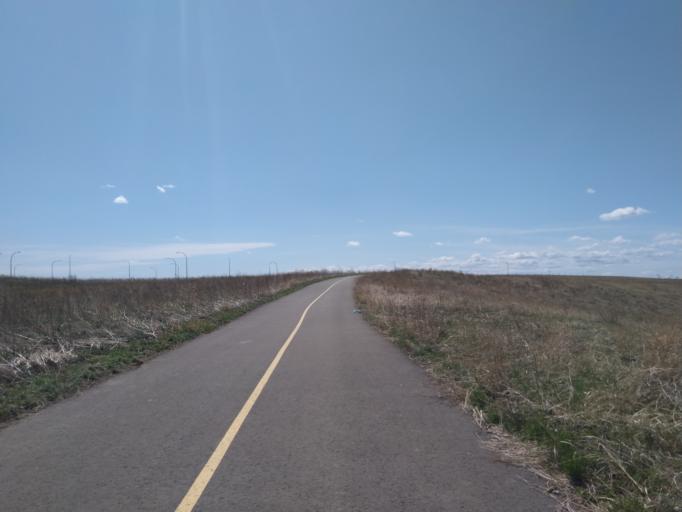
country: CA
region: Alberta
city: Chestermere
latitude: 51.0184
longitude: -113.9251
